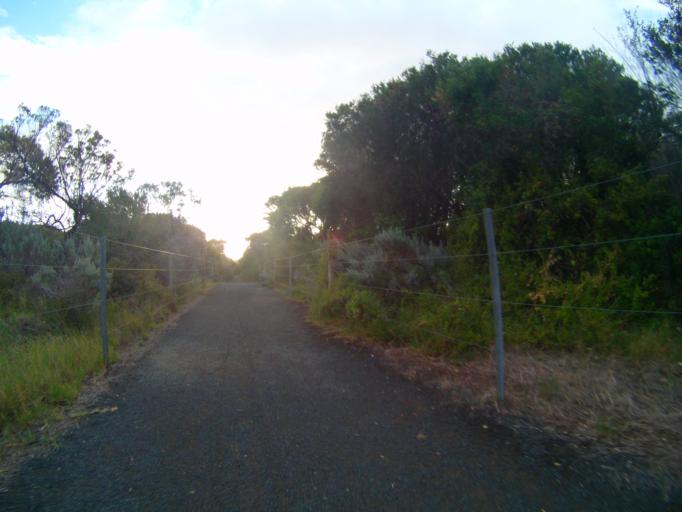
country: AU
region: Victoria
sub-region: Greater Geelong
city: Leopold
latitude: -38.2698
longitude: 144.5321
